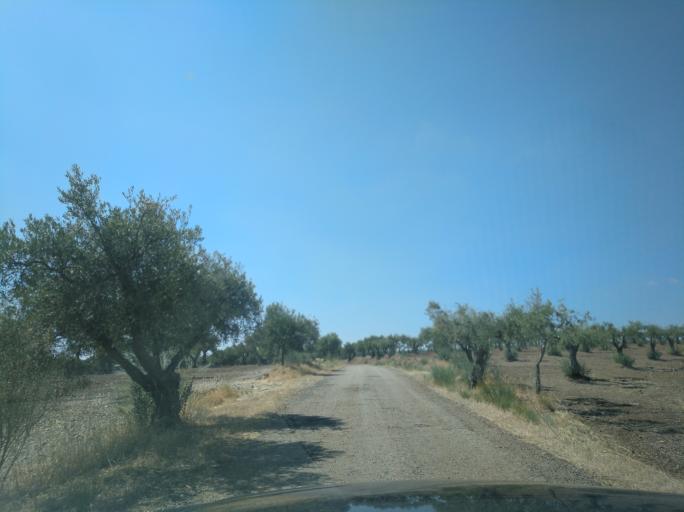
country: PT
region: Portalegre
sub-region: Campo Maior
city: Campo Maior
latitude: 39.0250
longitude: -7.1043
